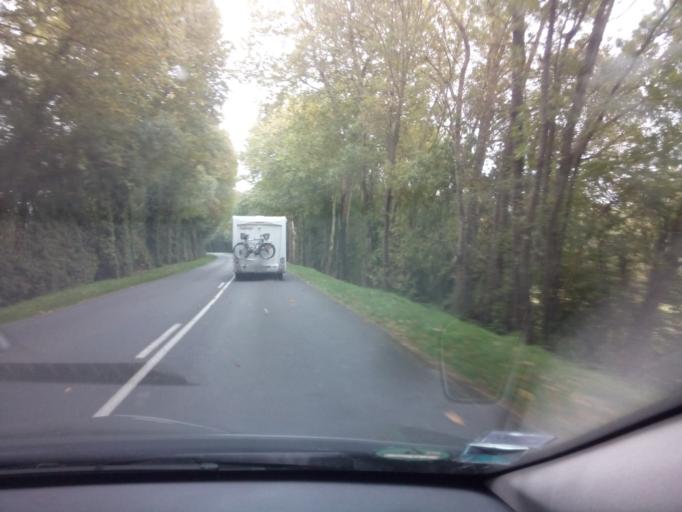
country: FR
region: Pays de la Loire
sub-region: Departement de Maine-et-Loire
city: Tierce
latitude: 47.6166
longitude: -0.4843
